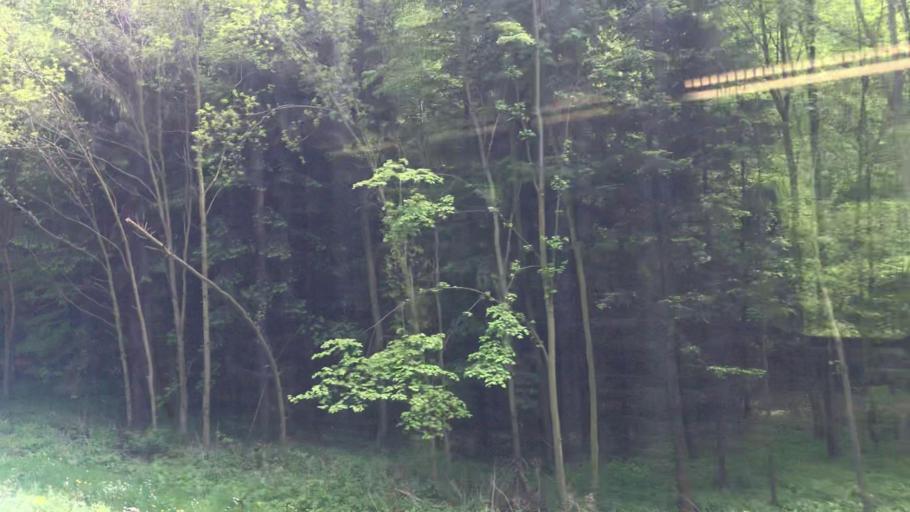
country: PL
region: Lower Silesian Voivodeship
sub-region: Powiat swidnicki
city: Swiebodzice
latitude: 50.8371
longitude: 16.3372
